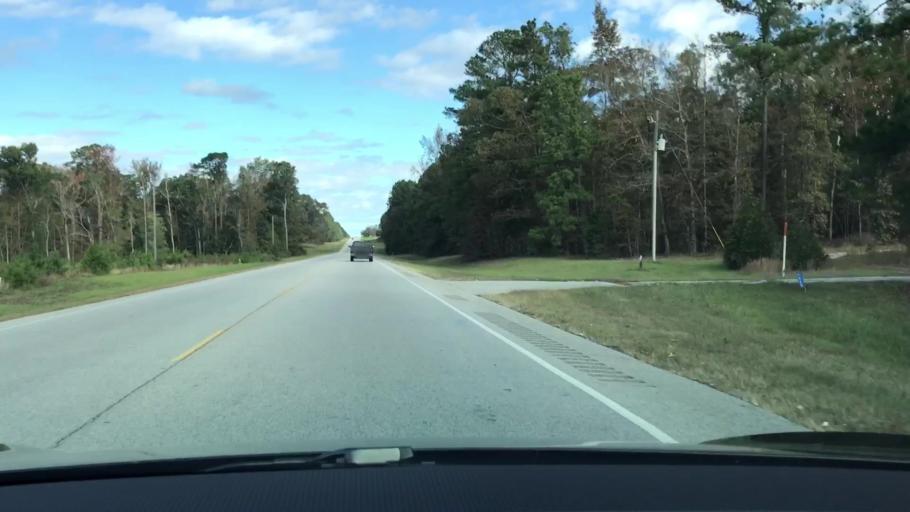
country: US
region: Georgia
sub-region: Jefferson County
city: Wadley
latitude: 32.9110
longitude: -82.3989
